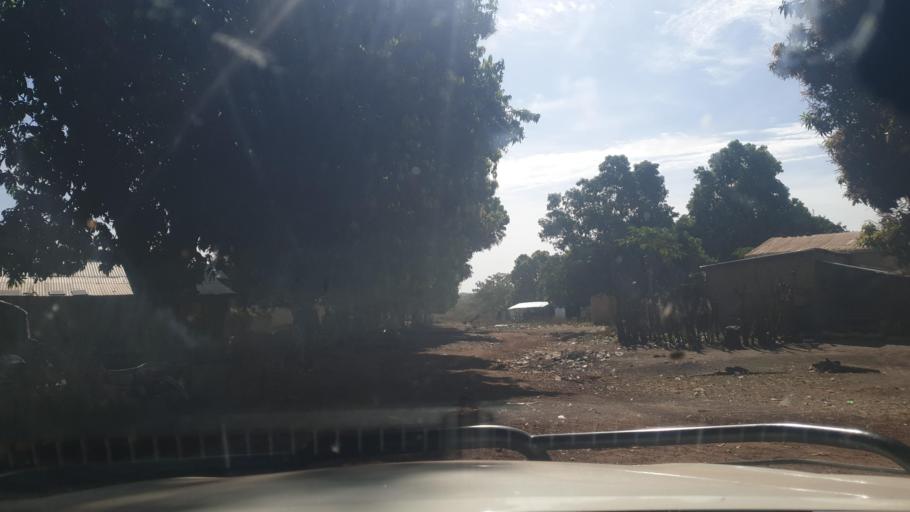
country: GN
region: Kankan
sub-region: Mandiana Prefecture
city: Mandiana
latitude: 10.4890
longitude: -8.0973
